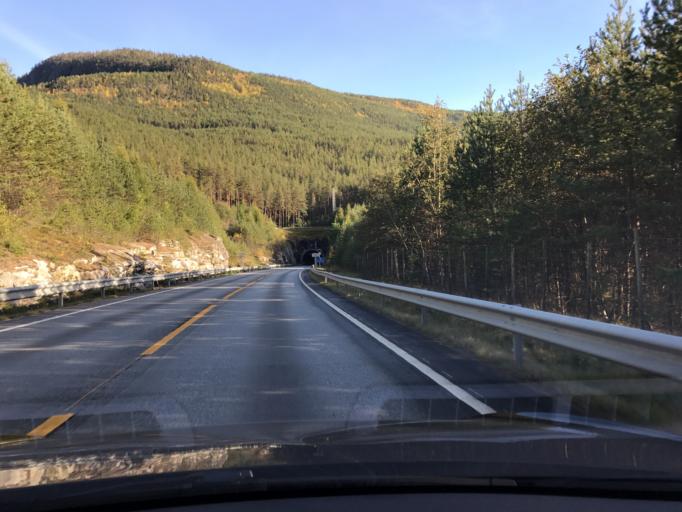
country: NO
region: Sogn og Fjordane
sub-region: Laerdal
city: Laerdalsoyri
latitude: 61.1809
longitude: 7.2973
